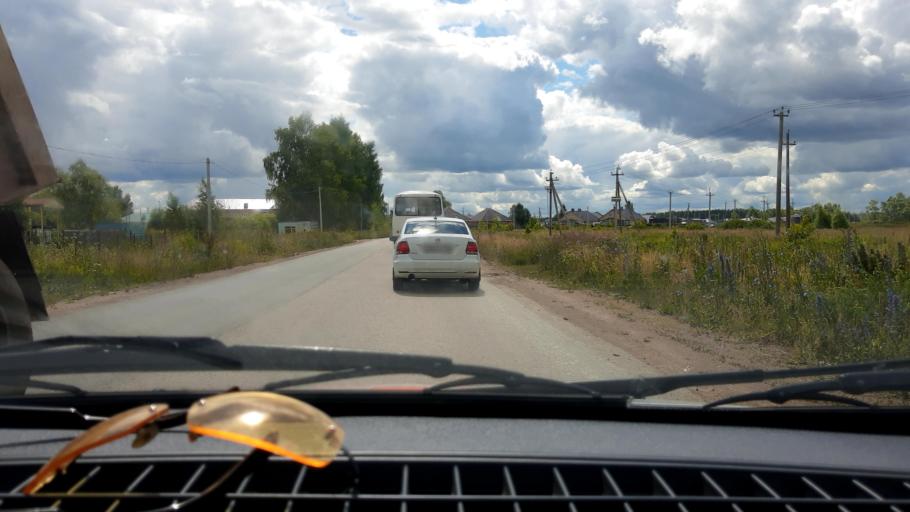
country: RU
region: Bashkortostan
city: Kabakovo
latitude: 54.6912
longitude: 56.1314
